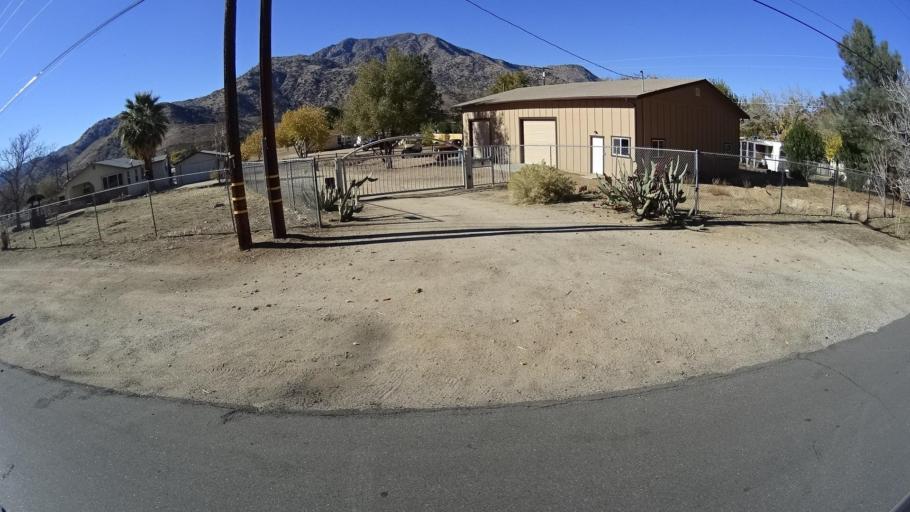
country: US
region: California
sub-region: Kern County
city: Kernville
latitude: 35.7352
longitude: -118.4149
